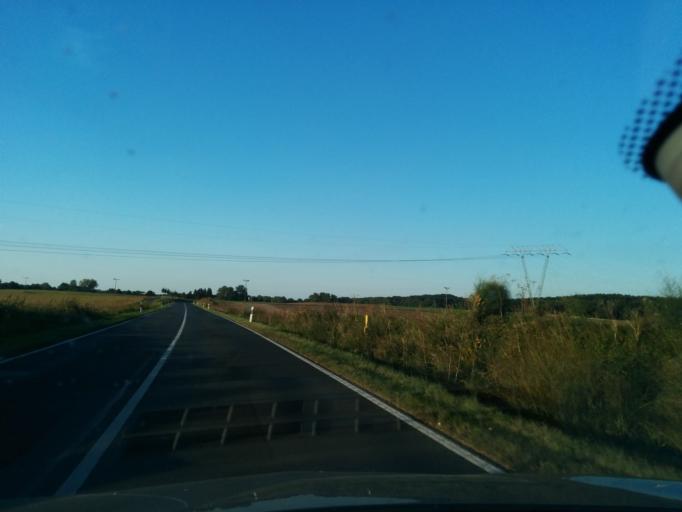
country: DE
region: Mecklenburg-Vorpommern
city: Loddin
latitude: 53.9282
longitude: 14.0324
